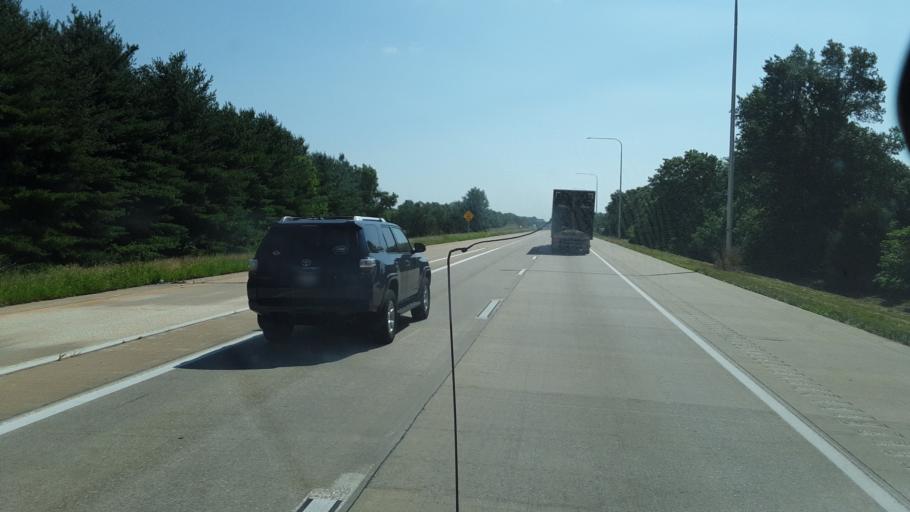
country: US
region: Illinois
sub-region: Effingham County
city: Teutopolis
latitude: 39.1496
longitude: -88.5041
